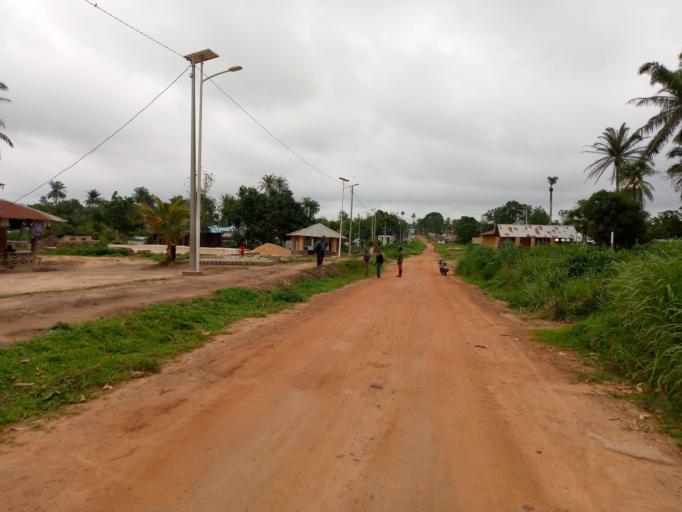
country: SL
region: Southern Province
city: Sumbuya
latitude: 7.5675
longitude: -12.0901
